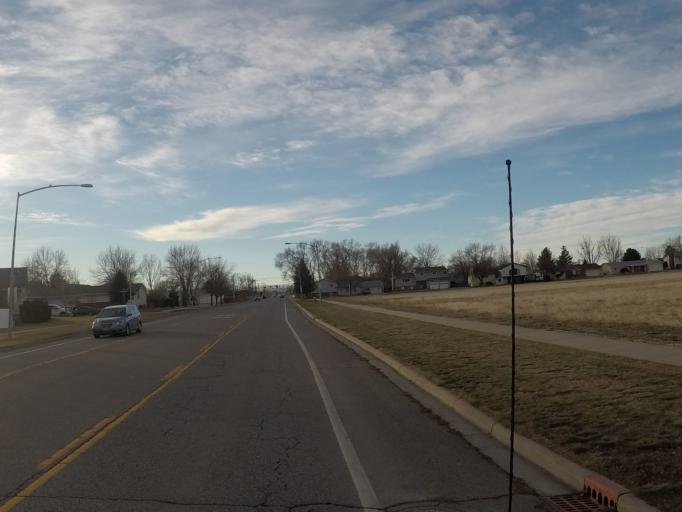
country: US
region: Montana
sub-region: Yellowstone County
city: Billings
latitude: 45.7729
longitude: -108.5970
